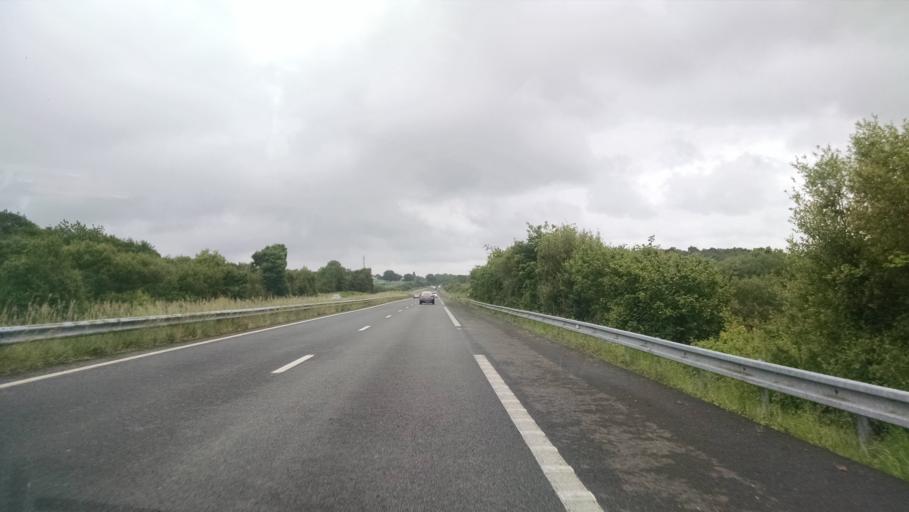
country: FR
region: Brittany
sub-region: Departement du Morbihan
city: Landaul
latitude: 47.7062
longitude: -3.0476
